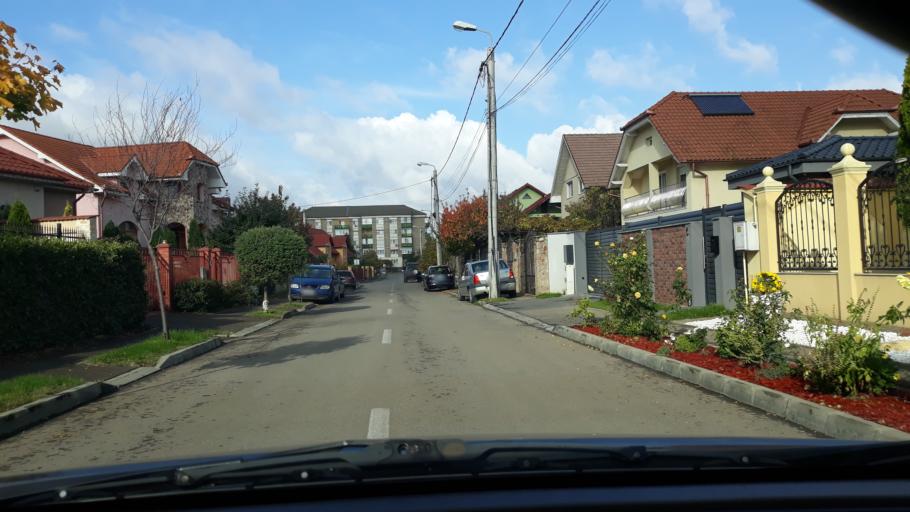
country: RO
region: Bihor
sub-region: Comuna Sanmartin
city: Sanmartin
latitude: 47.0288
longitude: 21.9497
